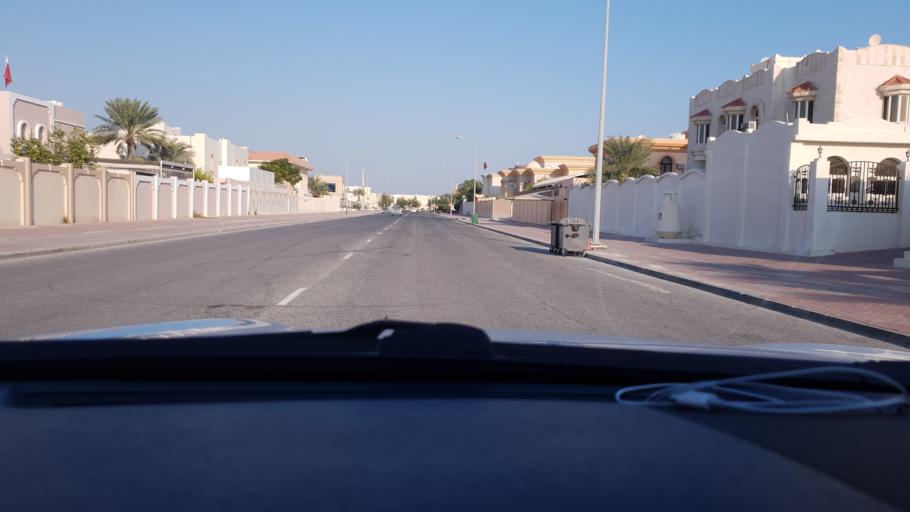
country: QA
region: Baladiyat ad Dawhah
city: Doha
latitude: 25.2372
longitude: 51.5604
